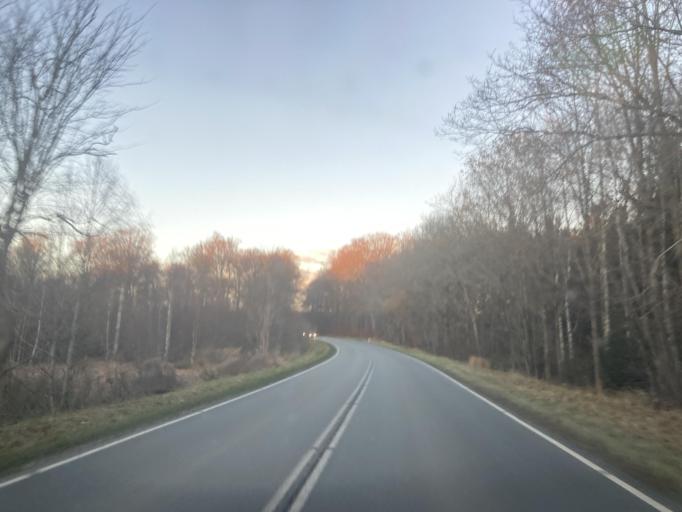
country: DK
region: Capital Region
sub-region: Gribskov Kommune
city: Graested
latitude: 56.0387
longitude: 12.2821
